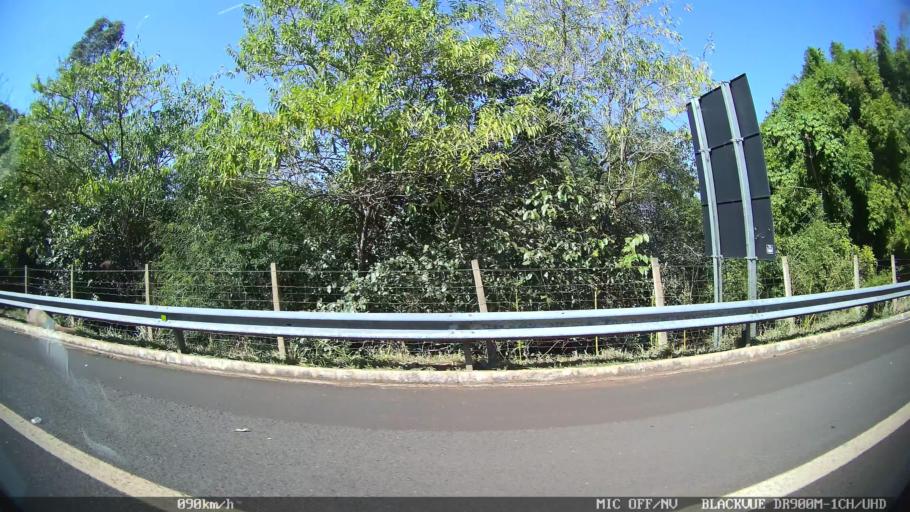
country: BR
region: Sao Paulo
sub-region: Batatais
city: Batatais
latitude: -20.7291
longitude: -47.5209
